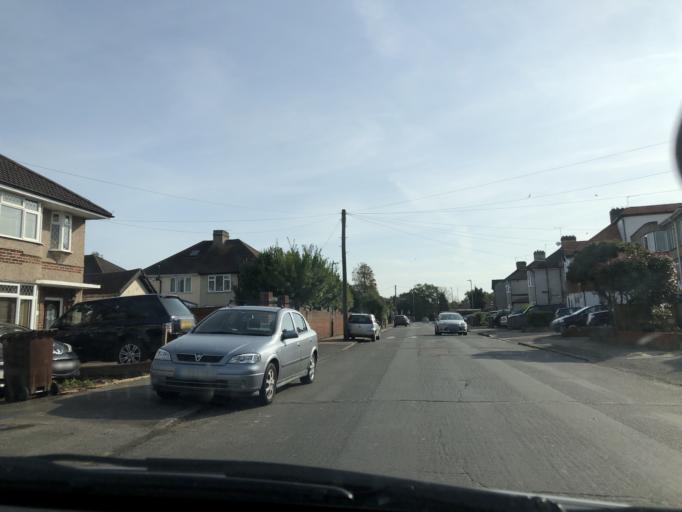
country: GB
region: England
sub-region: Kent
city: Dartford
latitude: 51.4412
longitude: 0.1883
